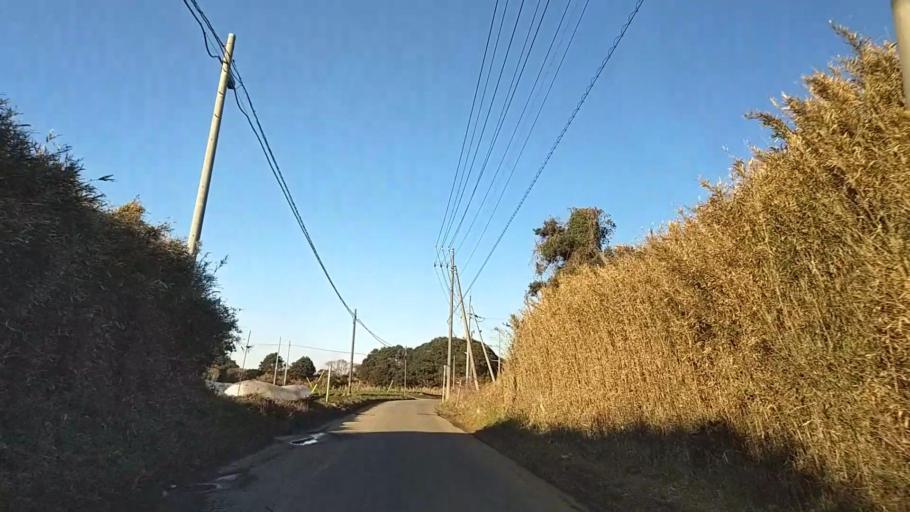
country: JP
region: Chiba
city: Asahi
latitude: 35.7309
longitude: 140.7380
